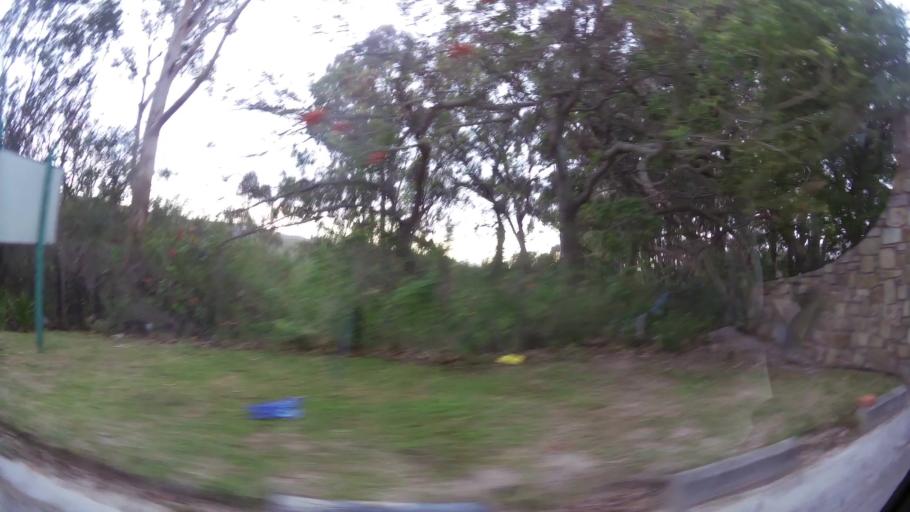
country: ZA
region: Eastern Cape
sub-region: Nelson Mandela Bay Metropolitan Municipality
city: Port Elizabeth
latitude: -33.9362
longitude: 25.5465
